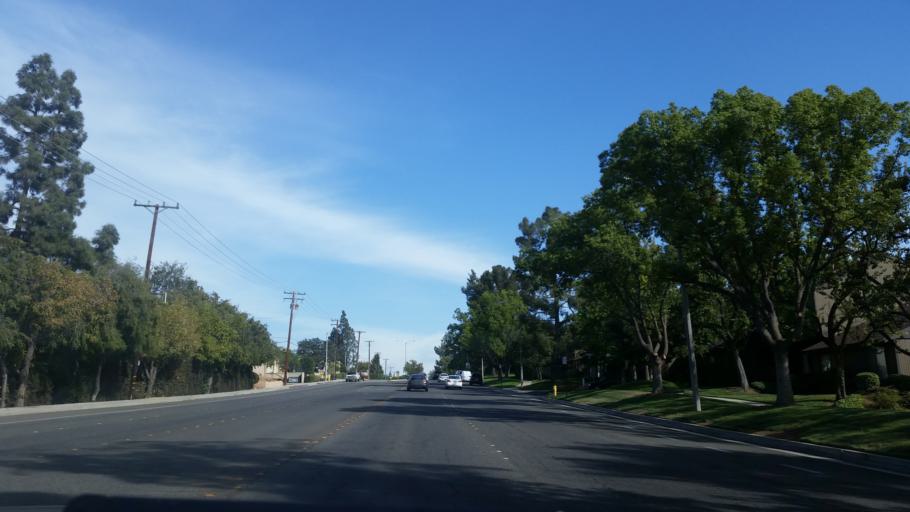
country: US
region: California
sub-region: Los Angeles County
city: San Dimas
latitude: 34.1260
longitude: -117.8148
